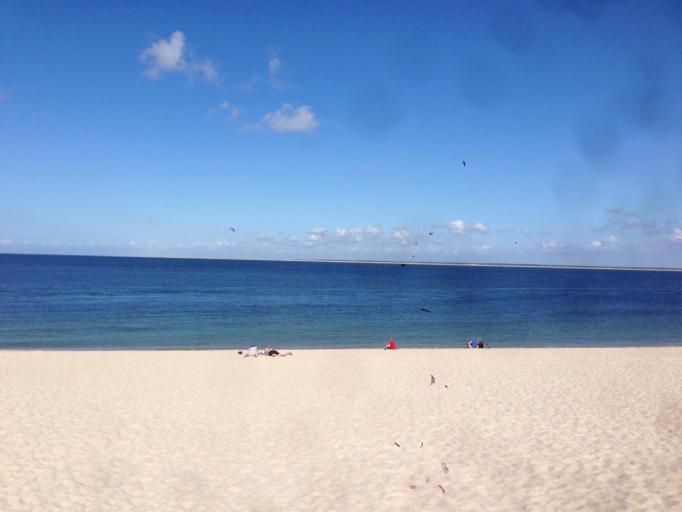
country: DE
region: Schleswig-Holstein
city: List
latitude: 55.0474
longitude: 8.4564
